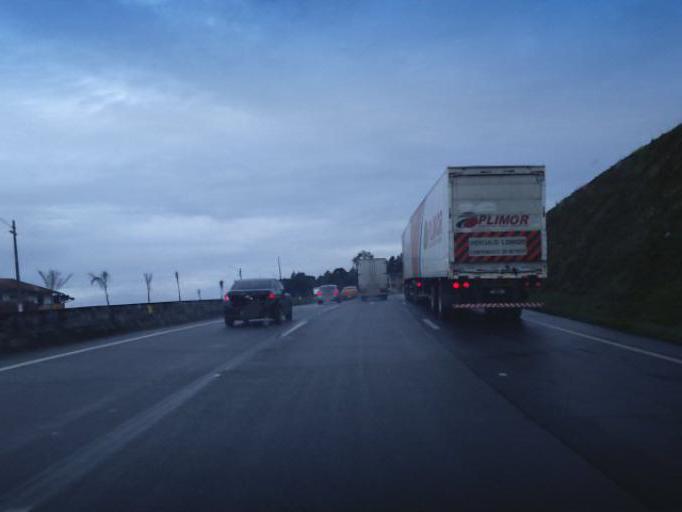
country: BR
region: Parana
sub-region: Sao Jose Dos Pinhais
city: Sao Jose dos Pinhais
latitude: -25.8462
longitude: -49.0665
